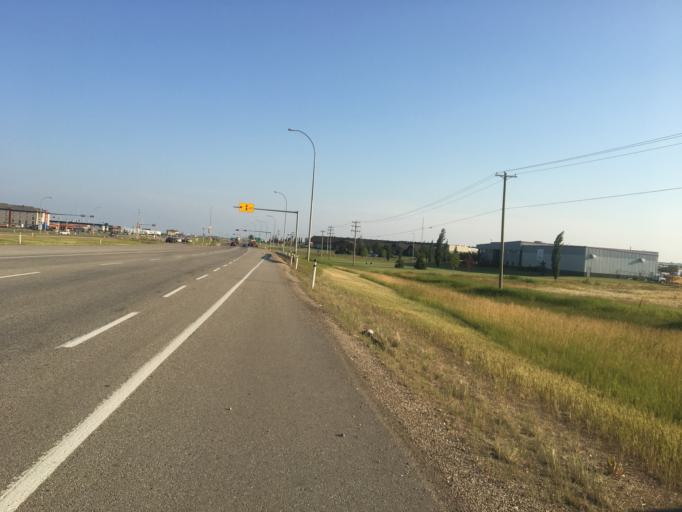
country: CA
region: Alberta
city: Grande Prairie
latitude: 55.2454
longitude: -118.7959
